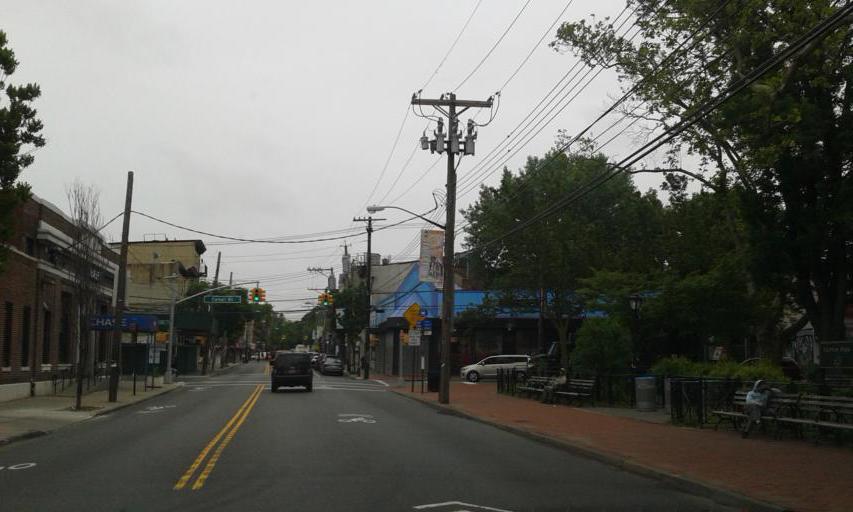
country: US
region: New Jersey
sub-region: Hudson County
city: Bayonne
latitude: 40.6273
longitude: -74.0758
